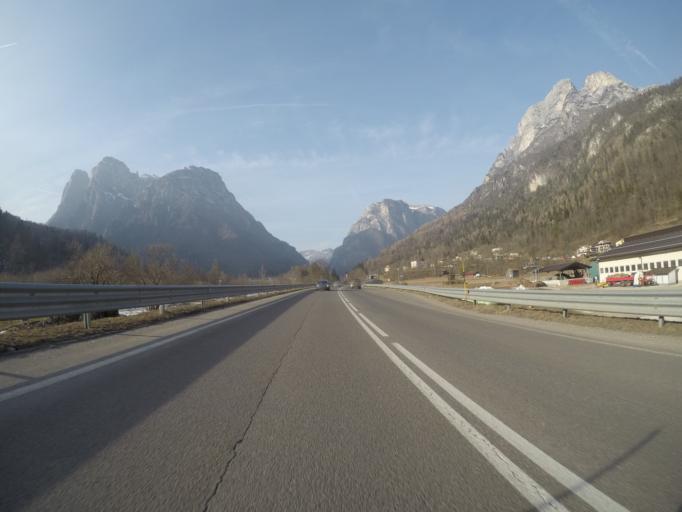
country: IT
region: Veneto
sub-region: Provincia di Belluno
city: Taibon Agordino
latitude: 46.2915
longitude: 12.0209
